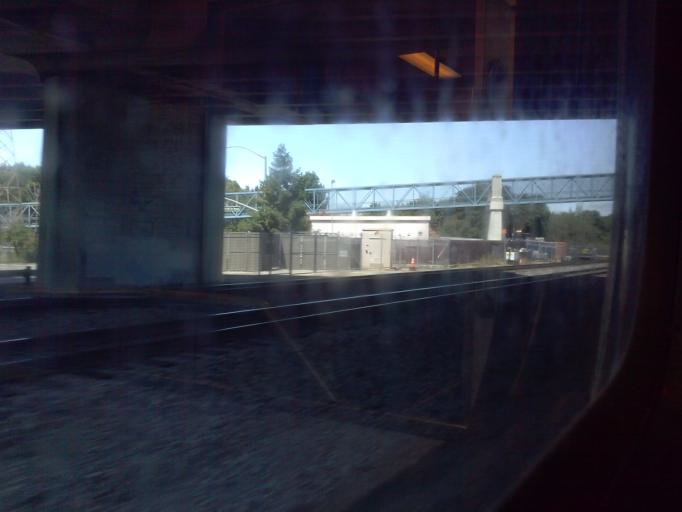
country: US
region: California
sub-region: Santa Clara County
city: Mountain View
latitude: 37.3914
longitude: -122.0684
